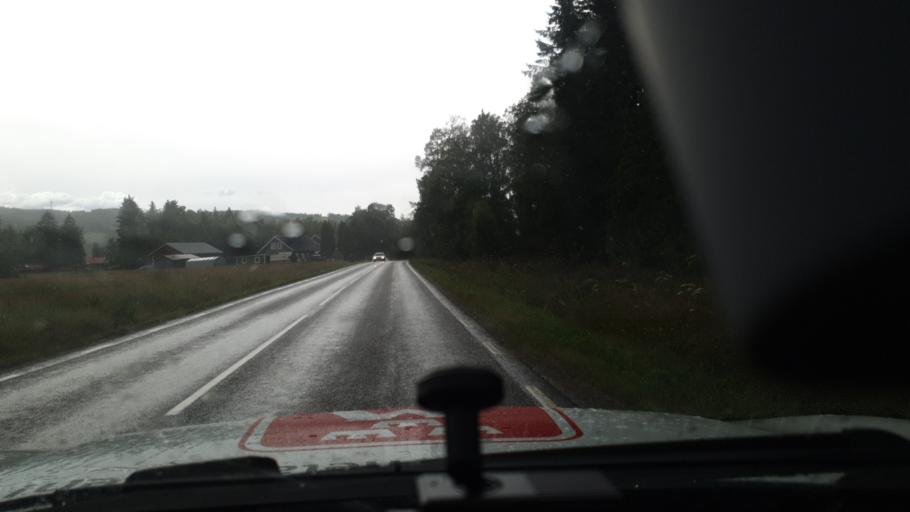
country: SE
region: Vaermland
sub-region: Sunne Kommun
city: Sunne
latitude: 59.7926
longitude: 13.0758
